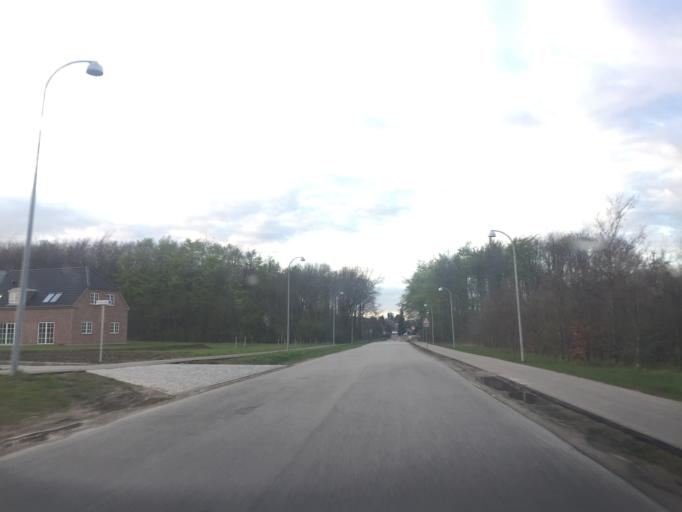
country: DK
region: Capital Region
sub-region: Hvidovre Kommune
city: Hvidovre
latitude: 55.6516
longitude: 12.4442
